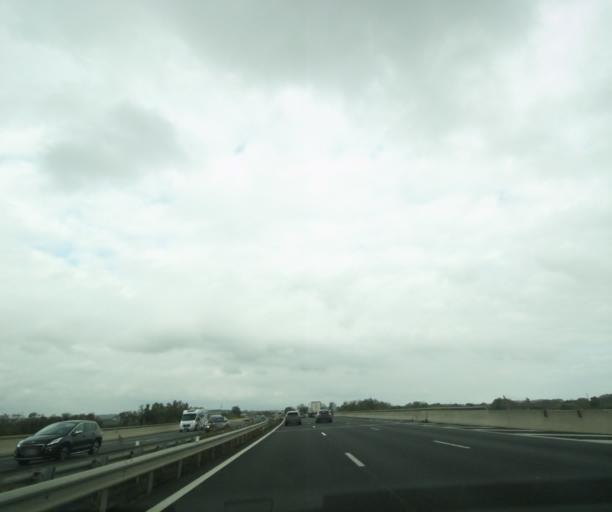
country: FR
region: Languedoc-Roussillon
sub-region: Departement de l'Herault
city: Florensac
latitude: 43.3801
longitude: 3.4471
